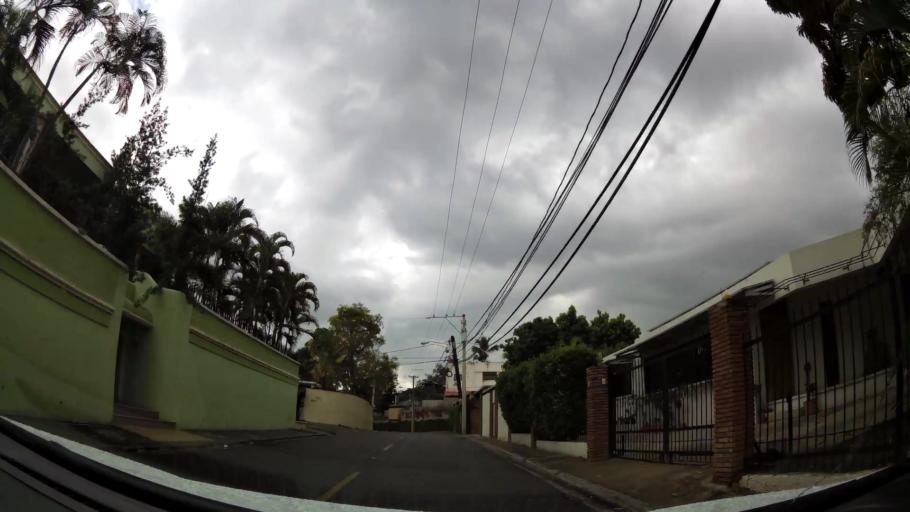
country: DO
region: Nacional
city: La Agustina
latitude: 18.4986
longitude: -69.9356
